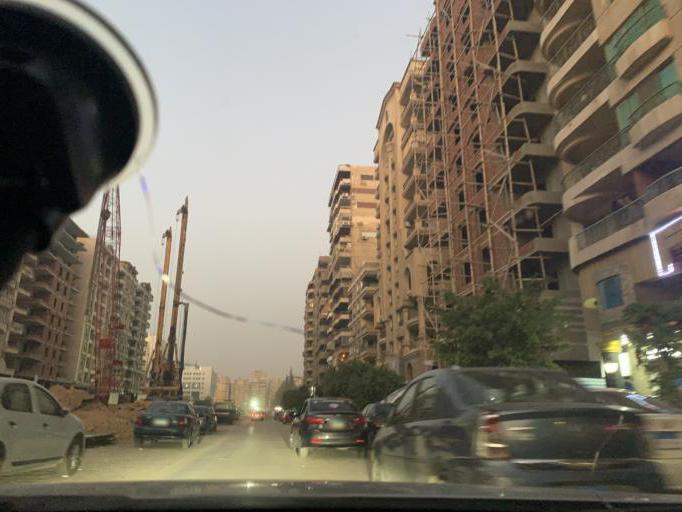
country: EG
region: Muhafazat al Qahirah
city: Cairo
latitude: 30.0626
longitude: 31.3425
